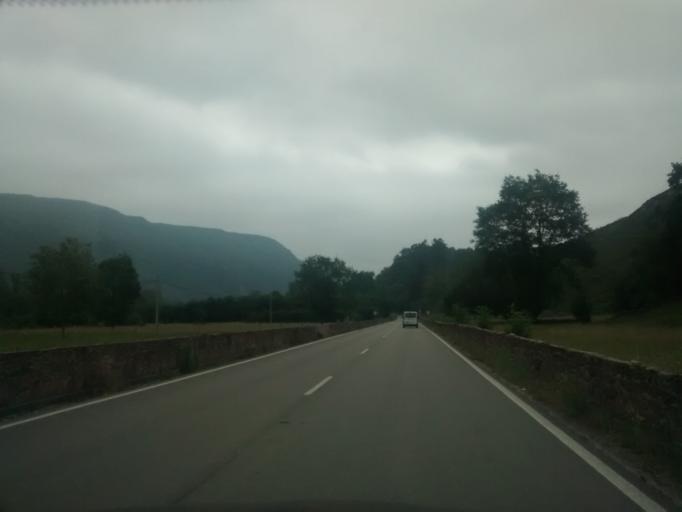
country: ES
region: Cantabria
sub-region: Provincia de Cantabria
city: Ruente
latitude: 43.2512
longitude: -4.2758
